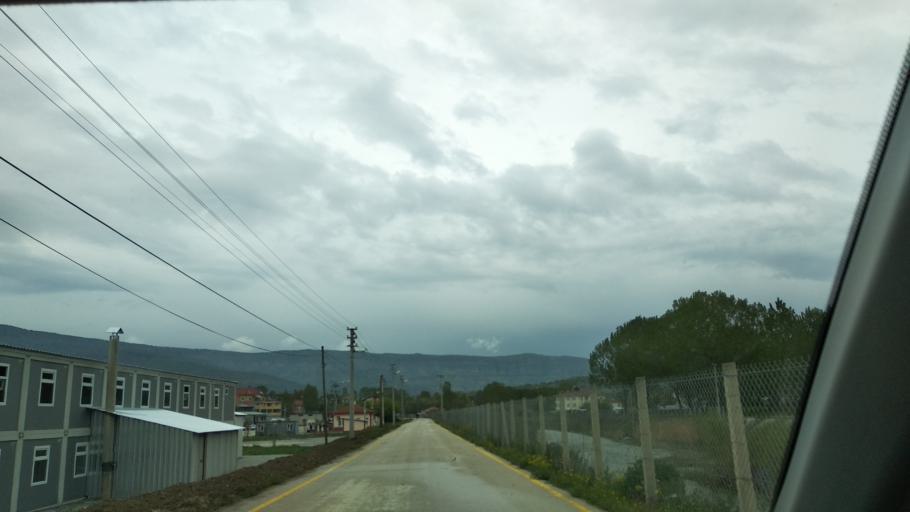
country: TR
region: Bolu
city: Seben
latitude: 40.4075
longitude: 31.5683
